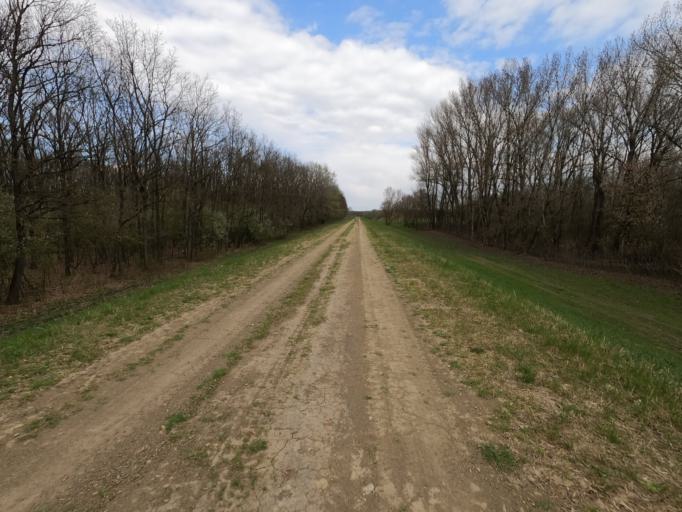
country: HU
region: Jasz-Nagykun-Szolnok
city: Turkeve
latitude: 47.0894
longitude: 20.7708
